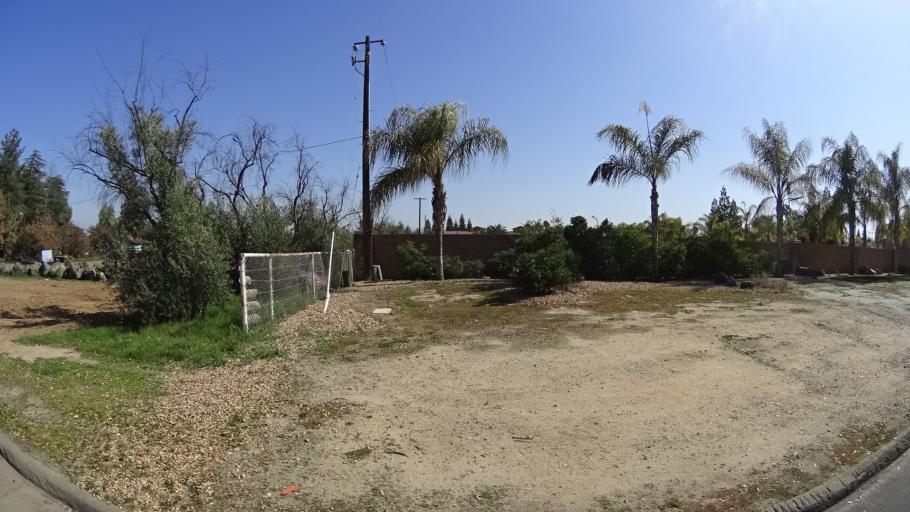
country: US
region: California
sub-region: Fresno County
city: Clovis
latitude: 36.8895
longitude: -119.7474
